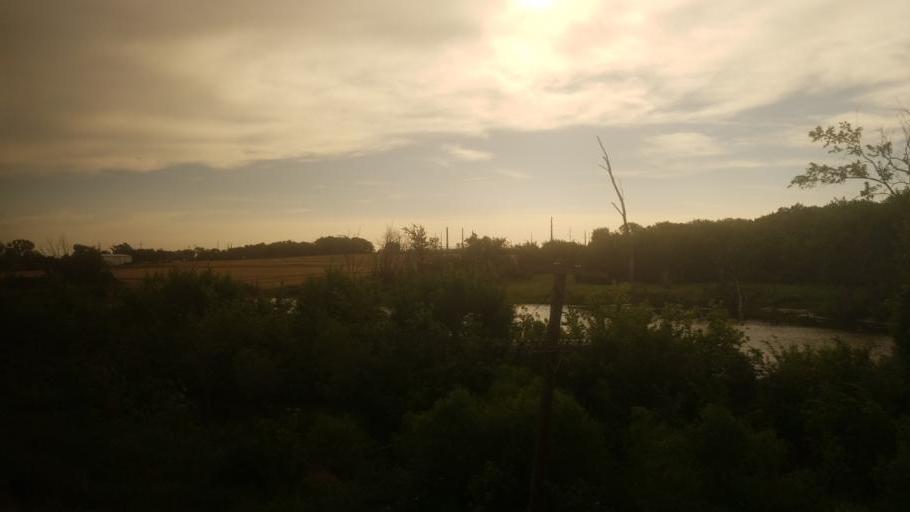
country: US
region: Kansas
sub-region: Osage County
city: Carbondale
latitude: 38.9246
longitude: -95.6924
